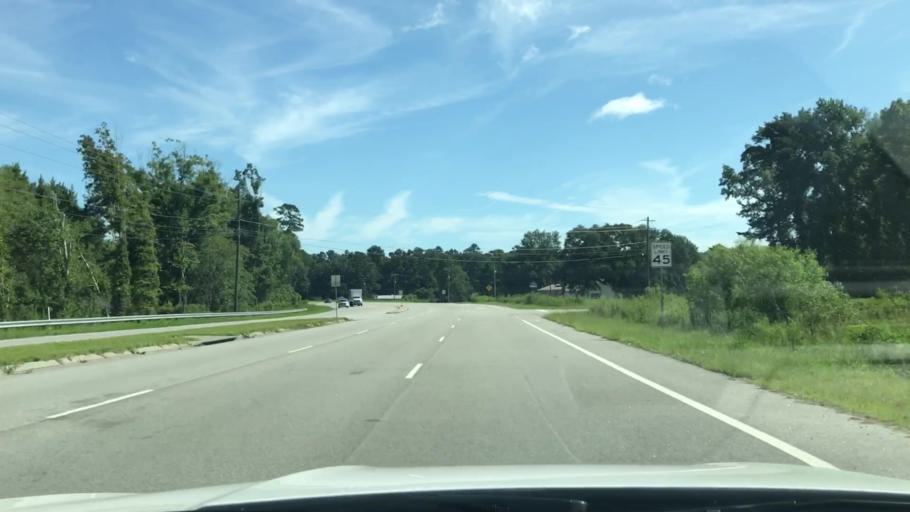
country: US
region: South Carolina
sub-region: Dorchester County
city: Centerville
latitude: 32.9499
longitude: -80.2038
